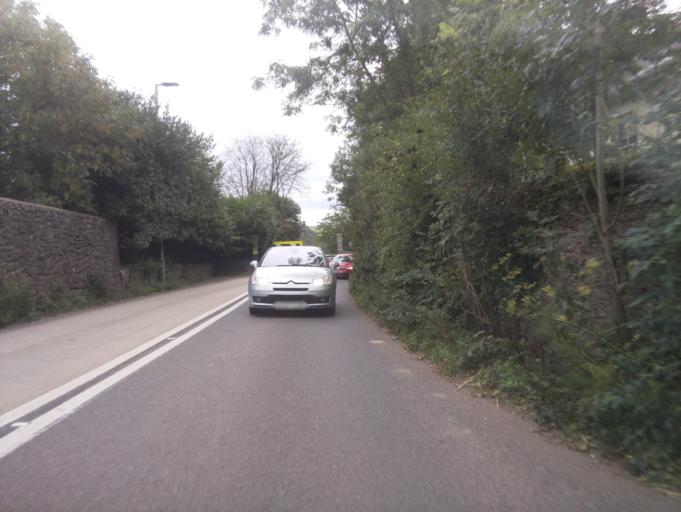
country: GB
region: England
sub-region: Devon
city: Totnes
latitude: 50.4334
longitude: -3.6615
